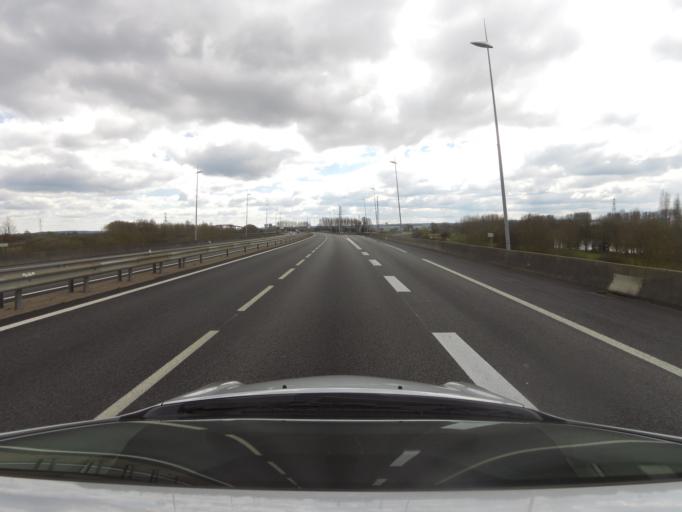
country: FR
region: Haute-Normandie
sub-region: Departement de la Seine-Maritime
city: Rogerville
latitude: 49.4840
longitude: 0.2632
